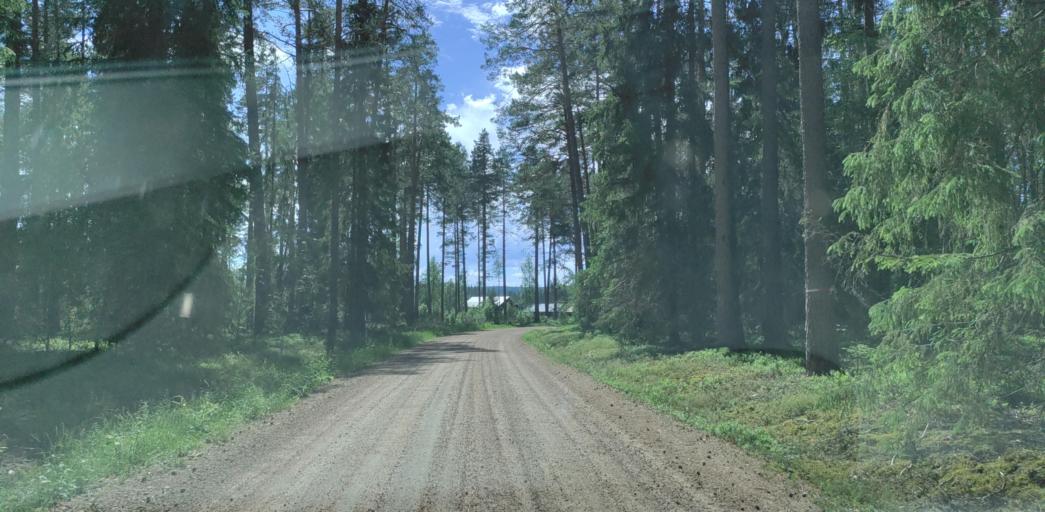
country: SE
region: Vaermland
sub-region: Munkfors Kommun
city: Munkfors
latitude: 59.9619
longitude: 13.5175
